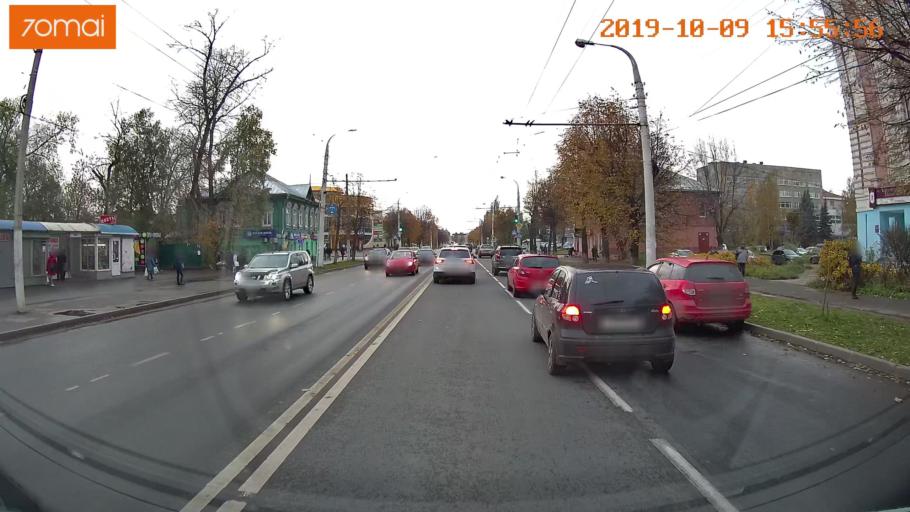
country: RU
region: Kostroma
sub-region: Kostromskoy Rayon
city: Kostroma
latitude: 57.7763
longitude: 40.9430
